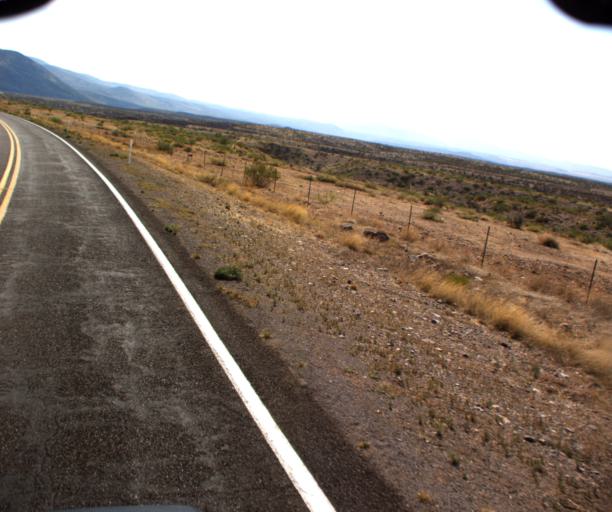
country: US
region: Arizona
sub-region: Greenlee County
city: Clifton
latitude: 32.9587
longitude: -109.2176
